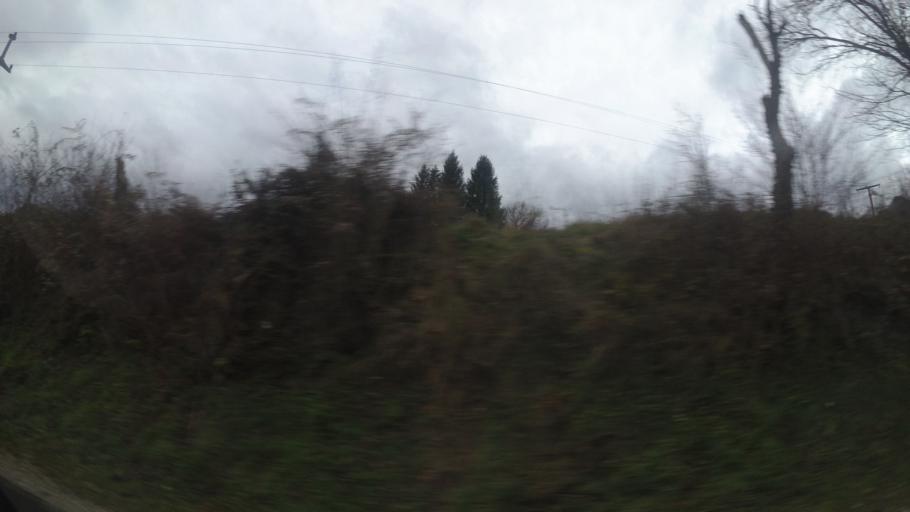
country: HR
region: Karlovacka
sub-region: Grad Karlovac
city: Karlovac
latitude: 45.3871
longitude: 15.5391
